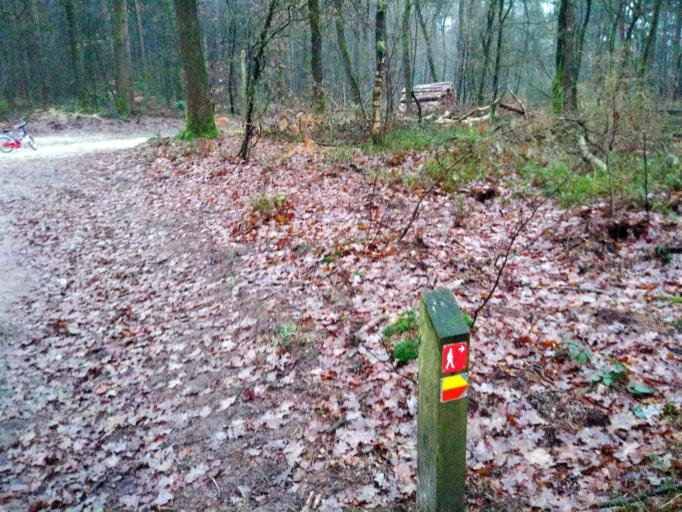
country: NL
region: Gelderland
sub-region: Gemeente Barneveld
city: Garderen
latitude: 52.2413
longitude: 5.6817
